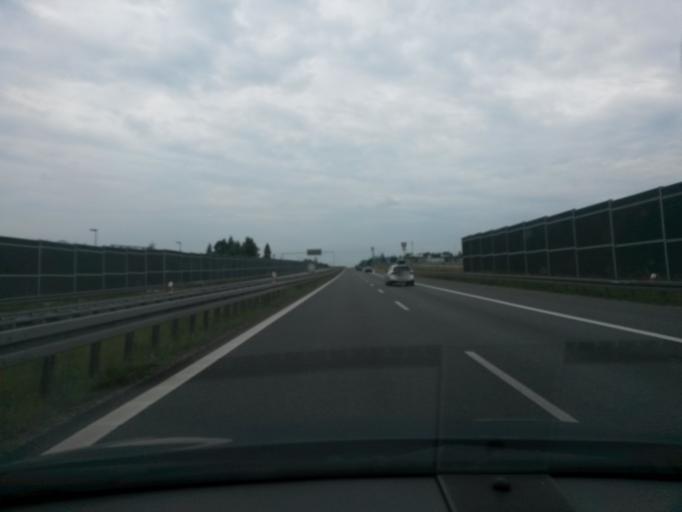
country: PL
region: Masovian Voivodeship
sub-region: Powiat zyrardowski
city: Radziejowice
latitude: 51.9963
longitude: 20.5506
